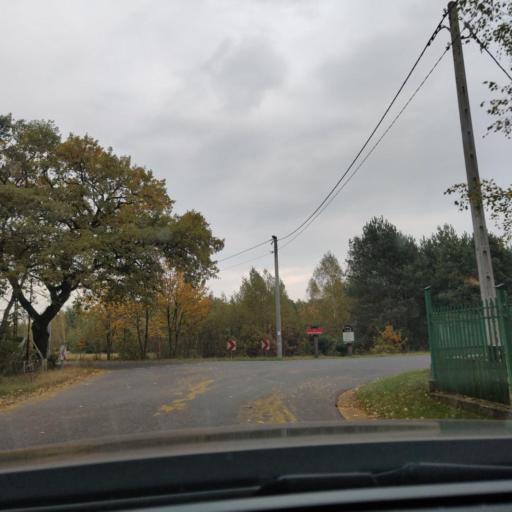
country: PL
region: Masovian Voivodeship
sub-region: Powiat sochaczewski
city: Brochow
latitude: 52.3067
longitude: 20.3229
